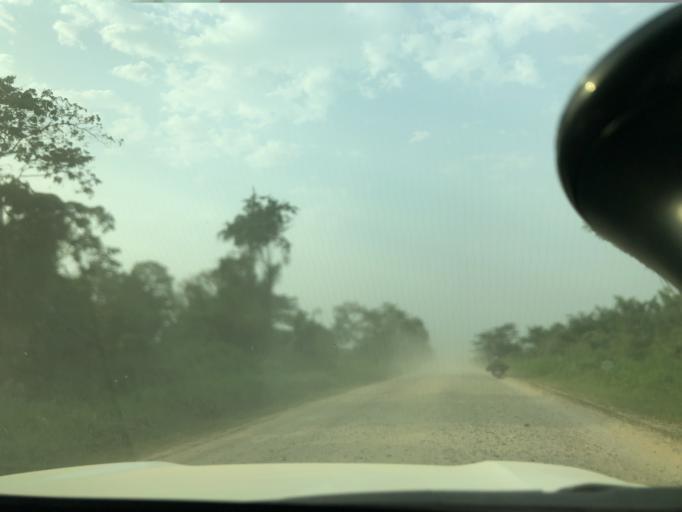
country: UG
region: Western Region
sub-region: Kasese District
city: Margherita
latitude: 0.2727
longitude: 29.6736
